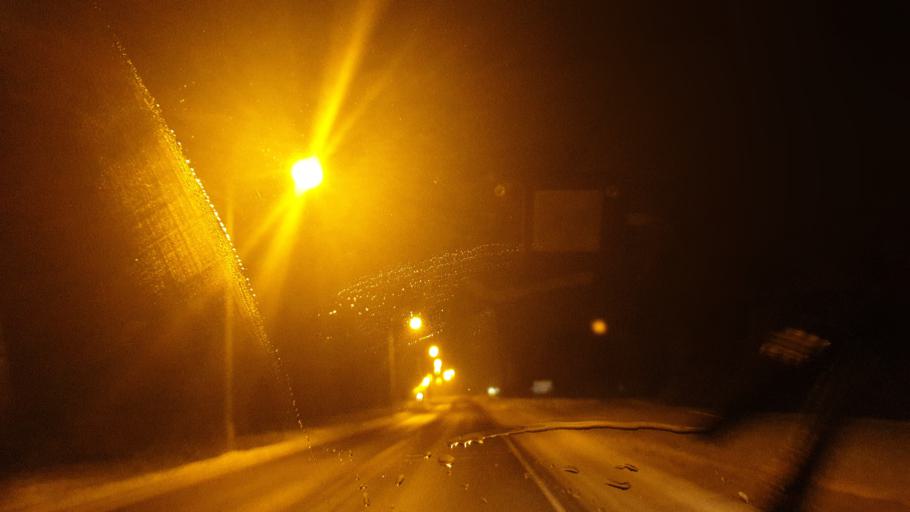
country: FI
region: Northern Ostrobothnia
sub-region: Oulunkaari
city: Ii
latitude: 65.2851
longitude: 25.3708
